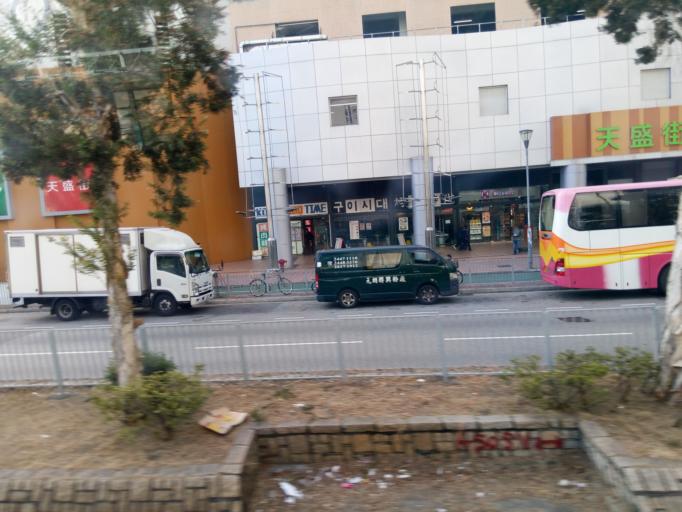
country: HK
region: Yuen Long
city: Yuen Long Kau Hui
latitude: 22.4488
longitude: 114.0032
